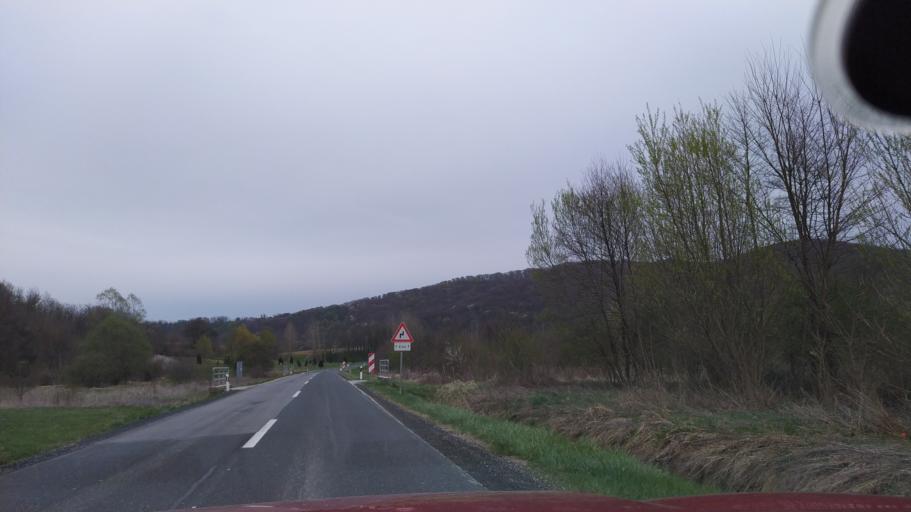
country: HR
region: Varazdinska
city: Jalzabet
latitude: 46.2180
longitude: 16.5277
